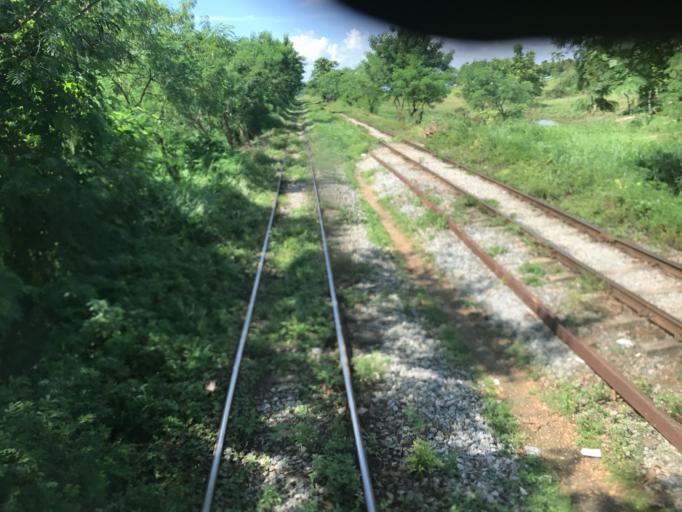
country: MM
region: Yangon
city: Yangon
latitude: 16.9611
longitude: 96.0871
